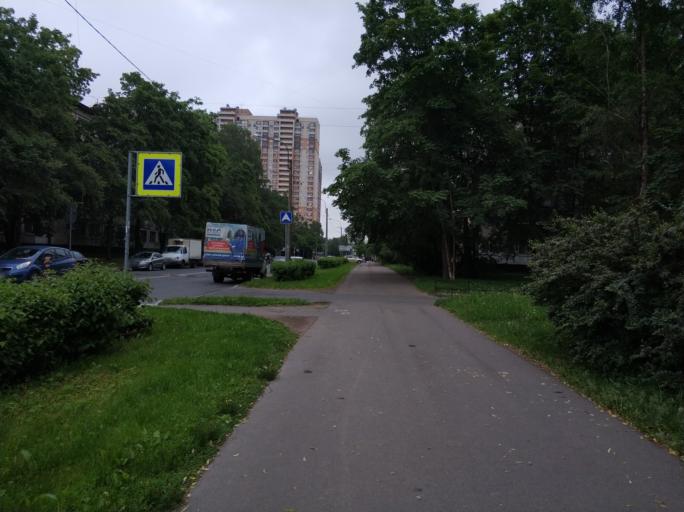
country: RU
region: St.-Petersburg
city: Grazhdanka
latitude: 60.0331
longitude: 30.3982
